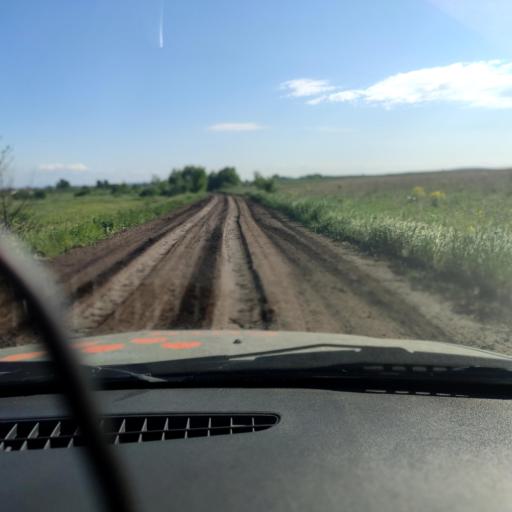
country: RU
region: Bashkortostan
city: Avdon
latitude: 54.5705
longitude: 55.8371
